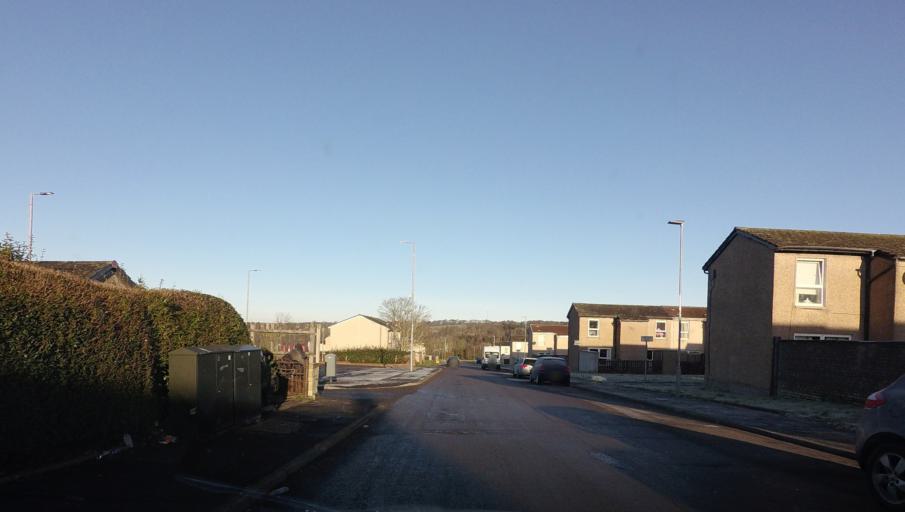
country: GB
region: Scotland
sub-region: North Lanarkshire
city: Newmains
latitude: 55.7894
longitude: -3.8851
